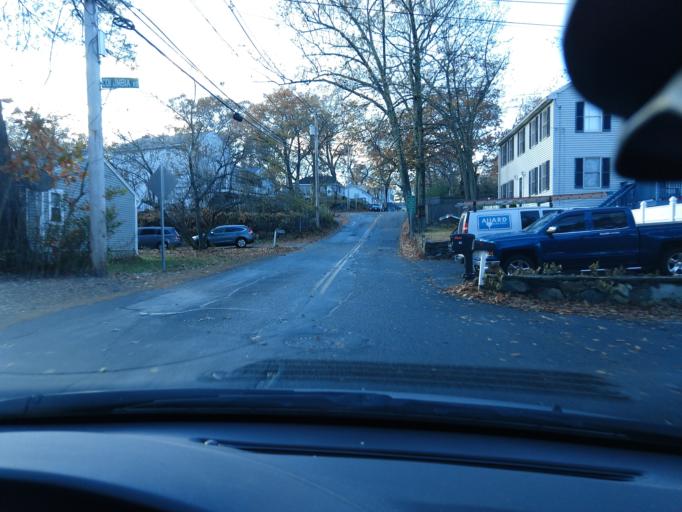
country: US
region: Massachusetts
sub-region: Middlesex County
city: Billerica
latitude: 42.5329
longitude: -71.2689
